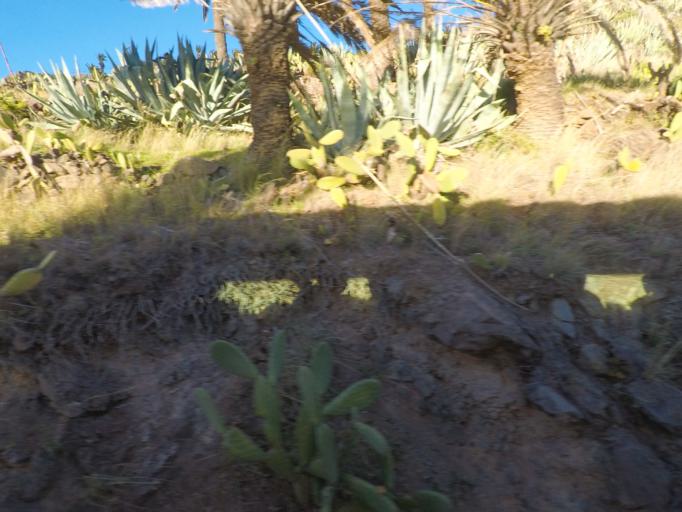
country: ES
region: Canary Islands
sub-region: Provincia de Santa Cruz de Tenerife
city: San Sebastian de la Gomera
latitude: 28.0965
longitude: -17.1609
